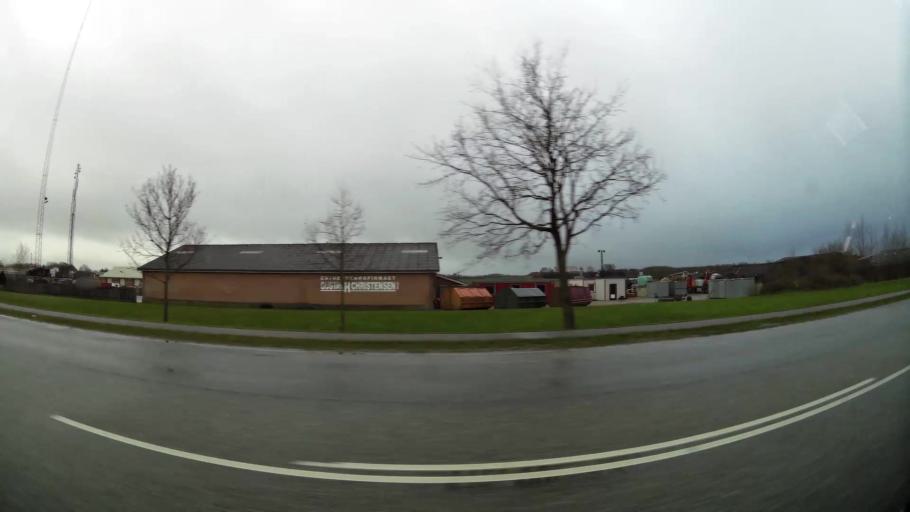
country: DK
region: Central Jutland
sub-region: Herning Kommune
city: Snejbjerg
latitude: 56.1345
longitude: 8.9158
